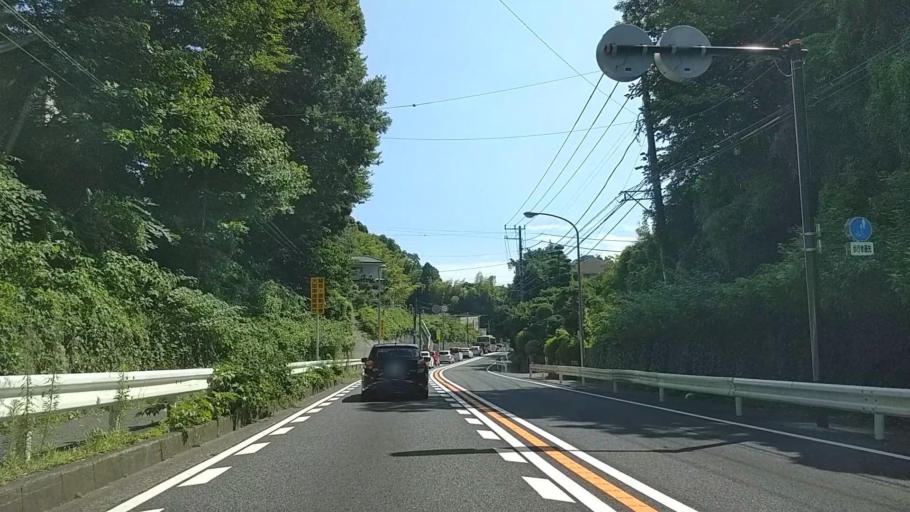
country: JP
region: Kanagawa
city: Fujisawa
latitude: 35.3502
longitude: 139.4906
